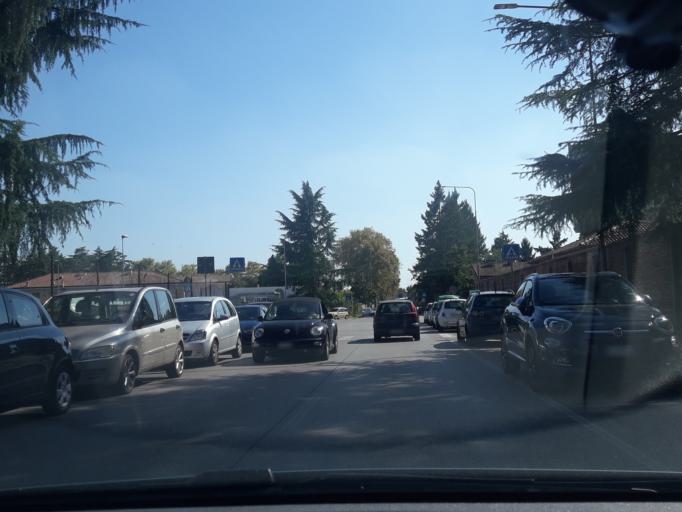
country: IT
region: Friuli Venezia Giulia
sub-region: Provincia di Udine
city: Feletto Umberto
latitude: 46.0795
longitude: 13.2237
